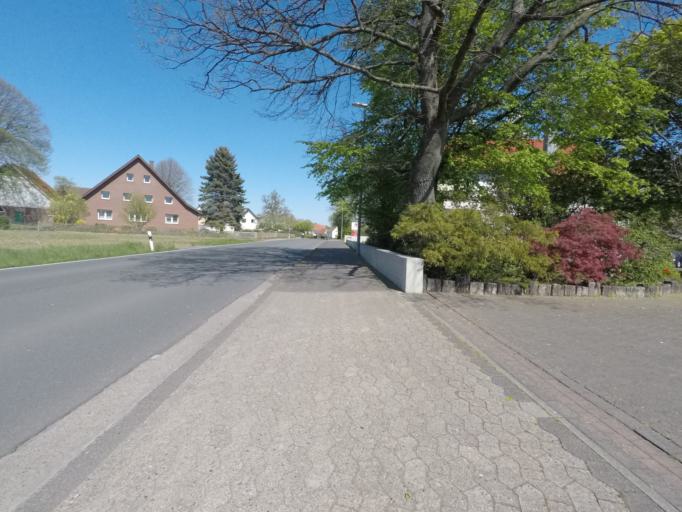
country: DE
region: North Rhine-Westphalia
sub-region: Regierungsbezirk Detmold
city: Leopoldshohe
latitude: 52.0618
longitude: 8.6804
